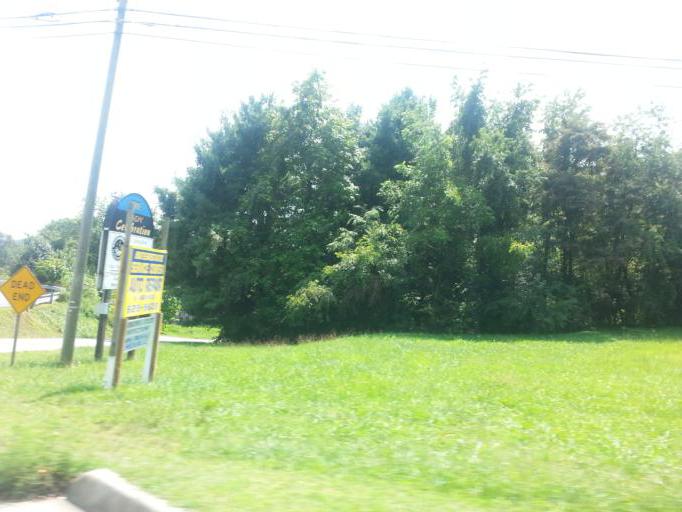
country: US
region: Virginia
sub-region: Washington County
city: Abingdon
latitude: 36.7149
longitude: -81.9400
